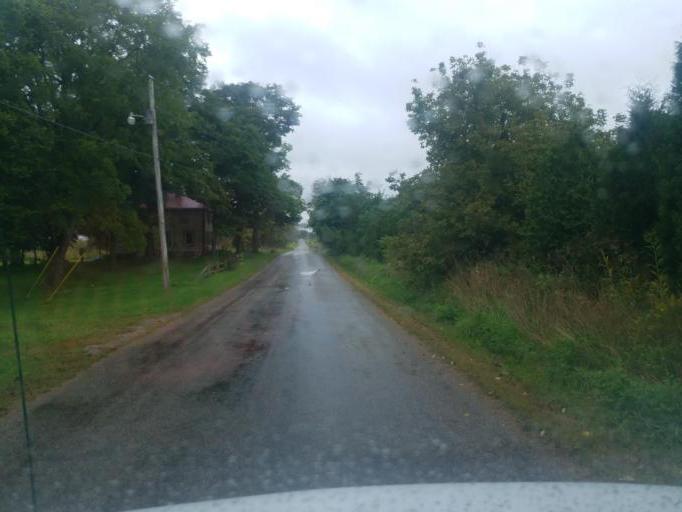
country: US
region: Ohio
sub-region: Wayne County
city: West Salem
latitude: 40.9194
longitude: -82.1186
